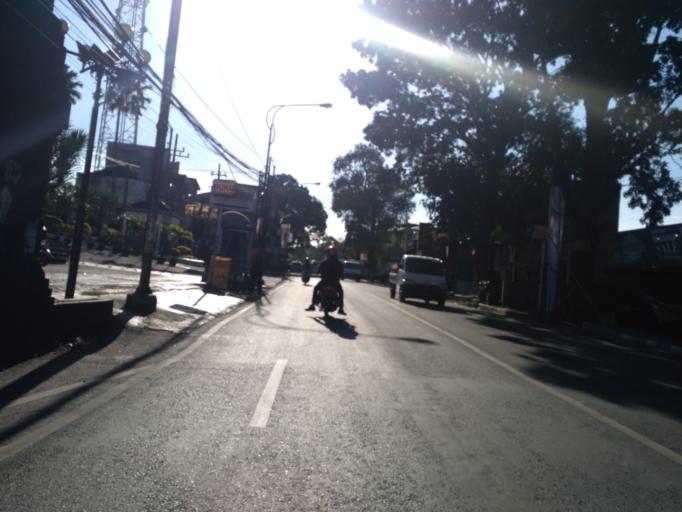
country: ID
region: East Java
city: Malang
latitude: -7.9205
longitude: 112.5943
